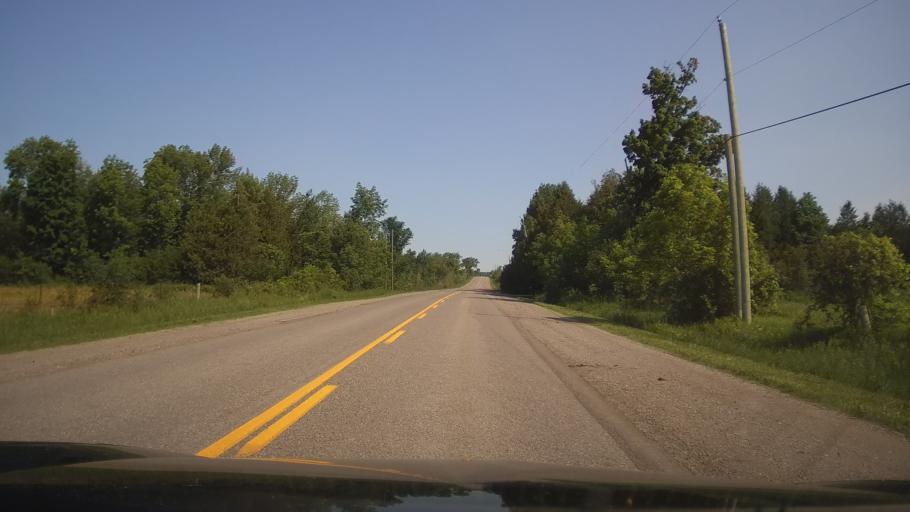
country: CA
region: Ontario
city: Omemee
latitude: 44.4391
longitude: -78.9212
